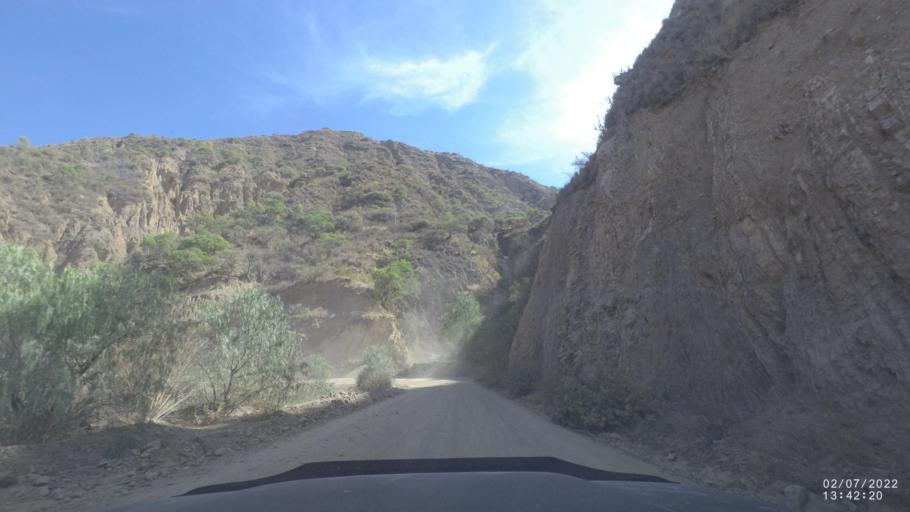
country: BO
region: Cochabamba
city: Irpa Irpa
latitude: -17.8000
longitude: -66.3556
